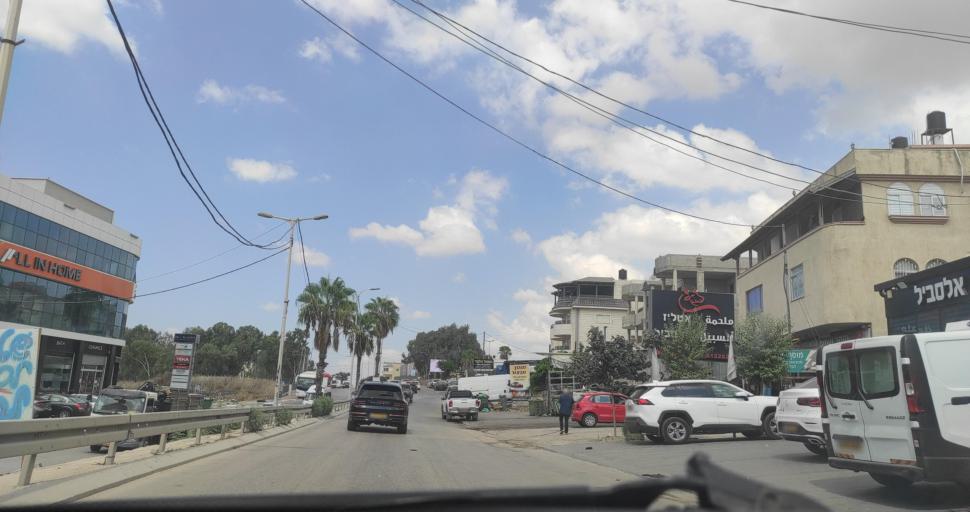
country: IL
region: Central District
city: Kafr Qasim
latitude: 32.1152
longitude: 34.9640
